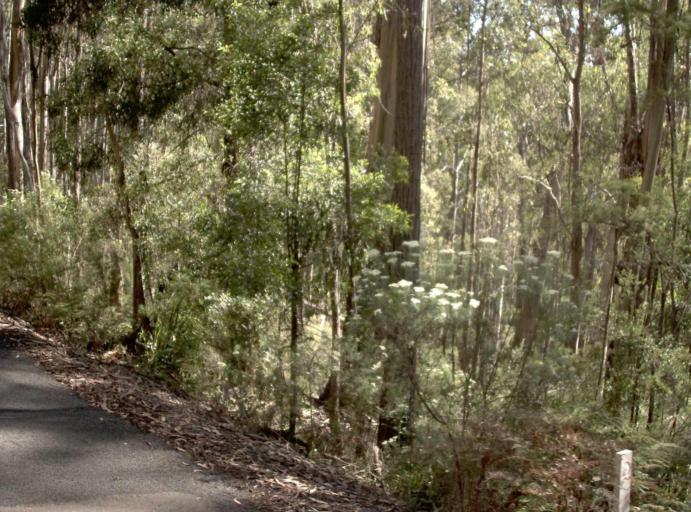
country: AU
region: New South Wales
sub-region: Bombala
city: Bombala
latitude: -37.3823
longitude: 148.6257
